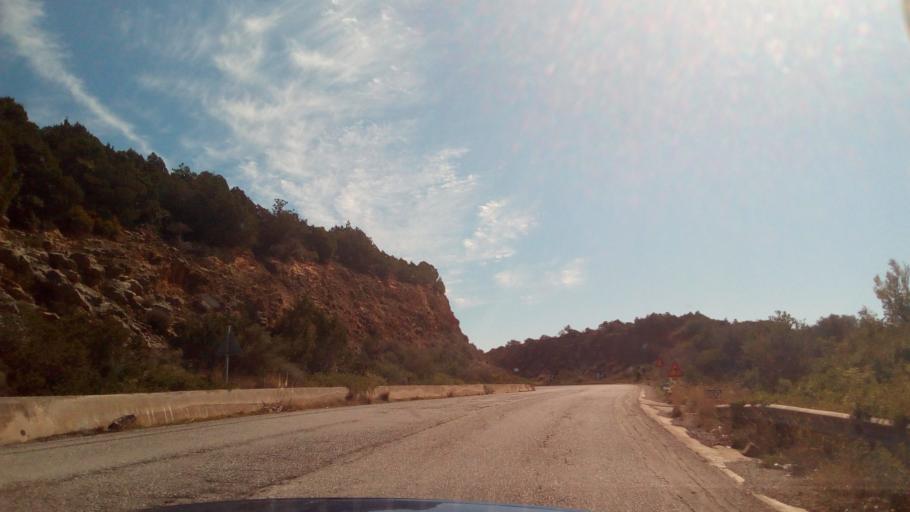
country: GR
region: West Greece
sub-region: Nomos Achaias
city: Selianitika
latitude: 38.3716
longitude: 22.1040
